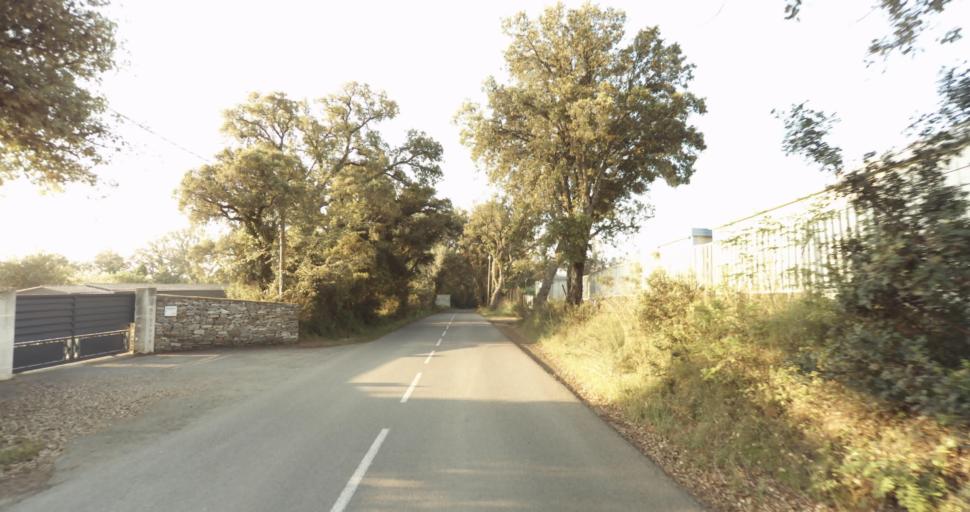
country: FR
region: Corsica
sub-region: Departement de la Haute-Corse
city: Biguglia
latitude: 42.6262
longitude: 9.4413
